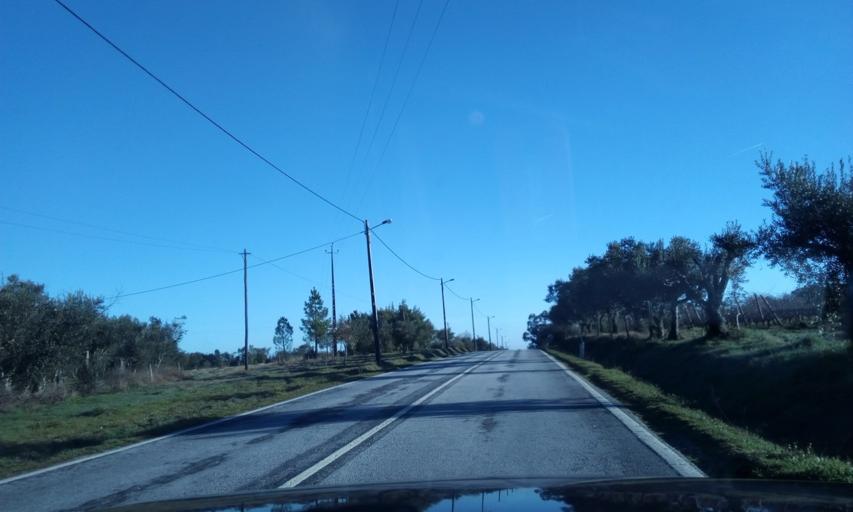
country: PT
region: Guarda
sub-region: Seia
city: Seia
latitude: 40.4773
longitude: -7.6690
